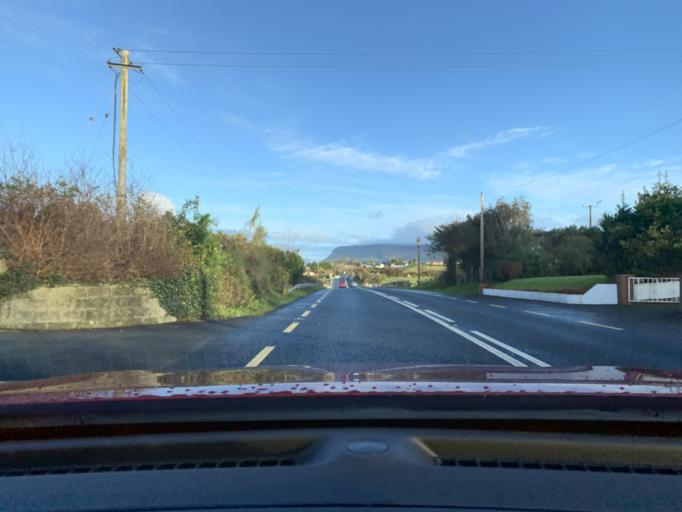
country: IE
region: Connaught
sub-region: Sligo
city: Sligo
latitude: 54.3016
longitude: -8.4726
